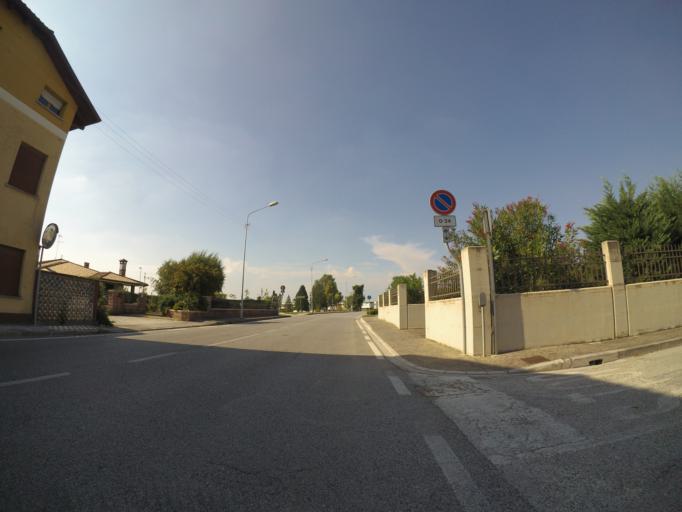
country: IT
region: Friuli Venezia Giulia
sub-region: Provincia di Udine
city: Pocenia
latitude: 45.8376
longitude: 13.0981
